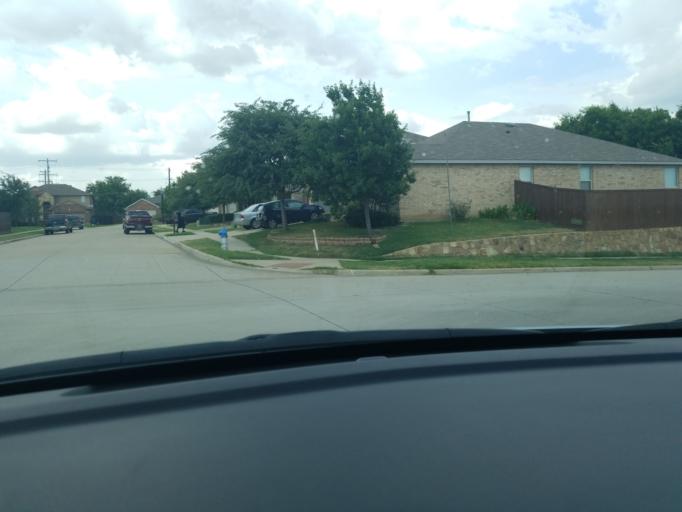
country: US
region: Texas
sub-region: Denton County
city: Little Elm
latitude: 33.2092
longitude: -96.9325
